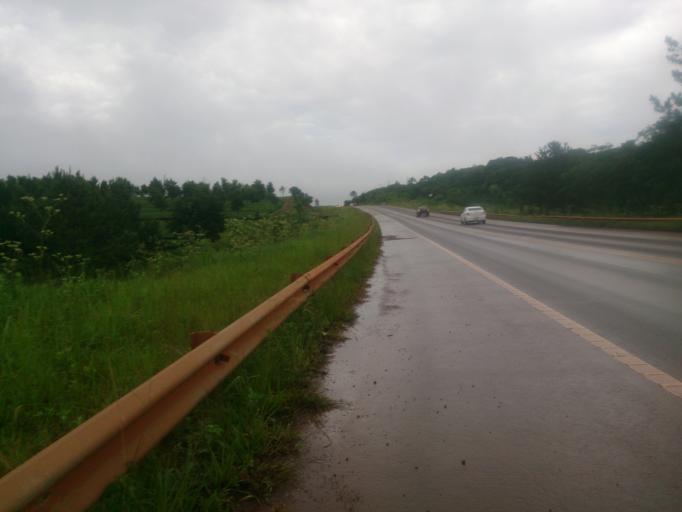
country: AR
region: Misiones
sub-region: Departamento de Obera
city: Obera
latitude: -27.4466
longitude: -55.0823
